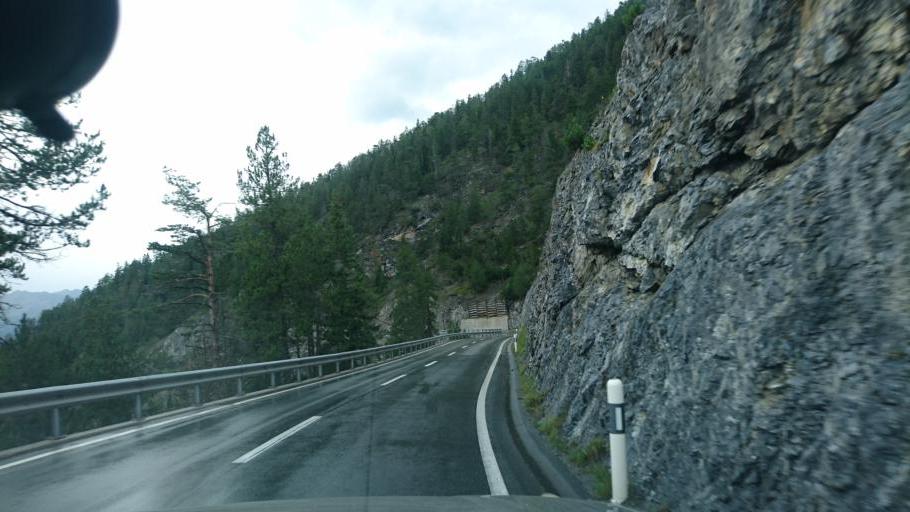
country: CH
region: Grisons
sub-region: Inn District
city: Zernez
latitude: 46.6877
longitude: 10.1449
